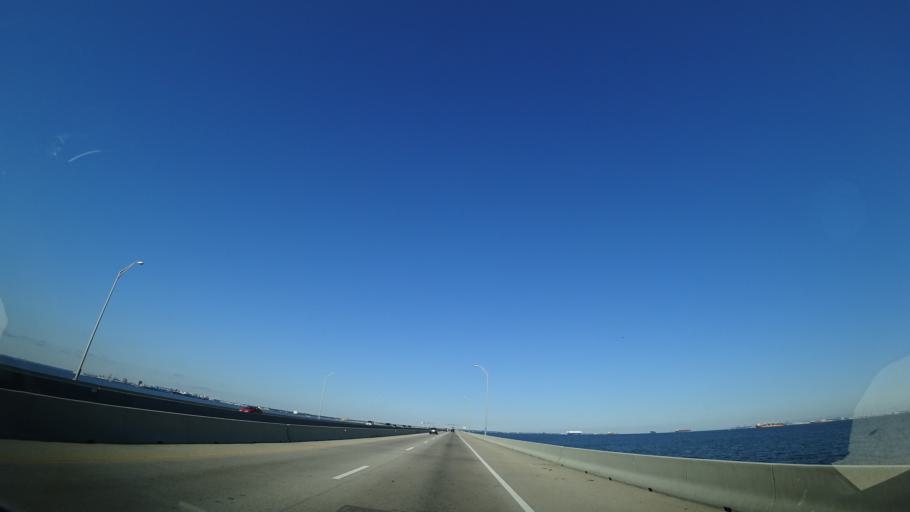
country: US
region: Virginia
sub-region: City of Newport News
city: Newport News
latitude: 36.9271
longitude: -76.4089
